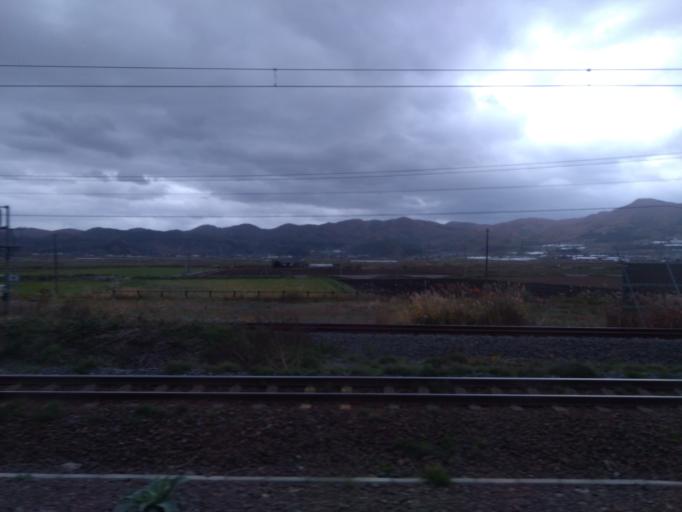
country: JP
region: Hokkaido
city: Nanae
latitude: 41.9041
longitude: 140.6514
